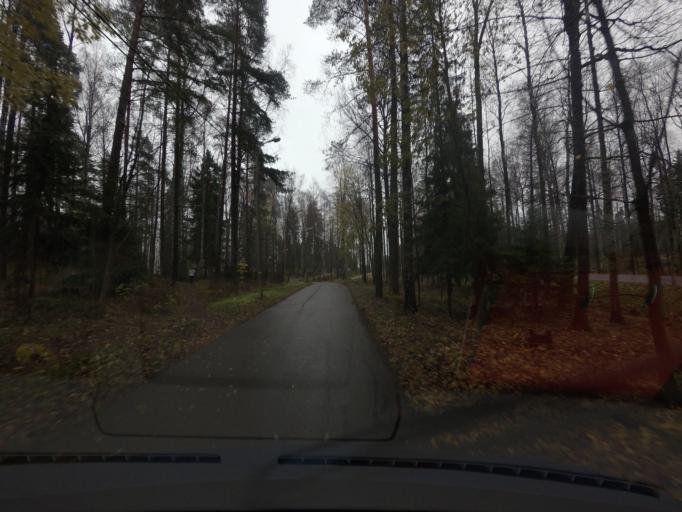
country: FI
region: Uusimaa
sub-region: Helsinki
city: Kilo
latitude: 60.2289
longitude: 24.7560
